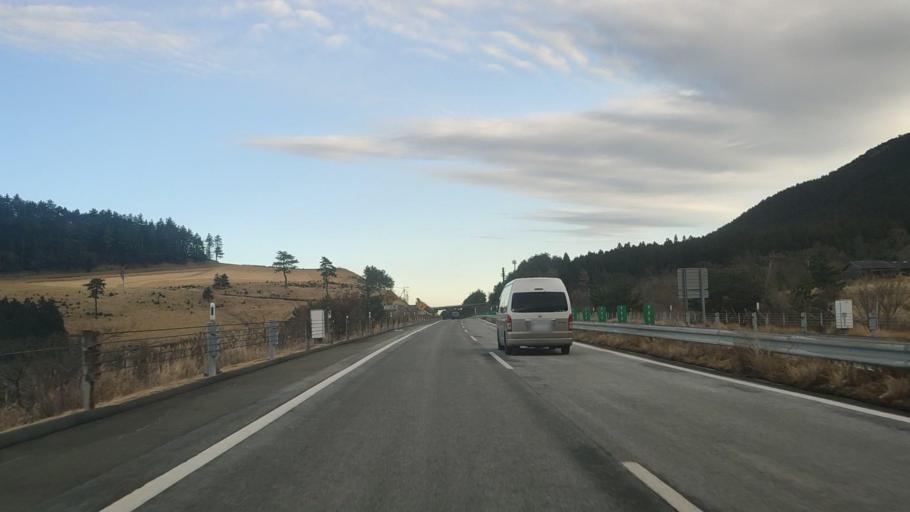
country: JP
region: Oita
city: Beppu
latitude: 33.3171
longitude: 131.4103
